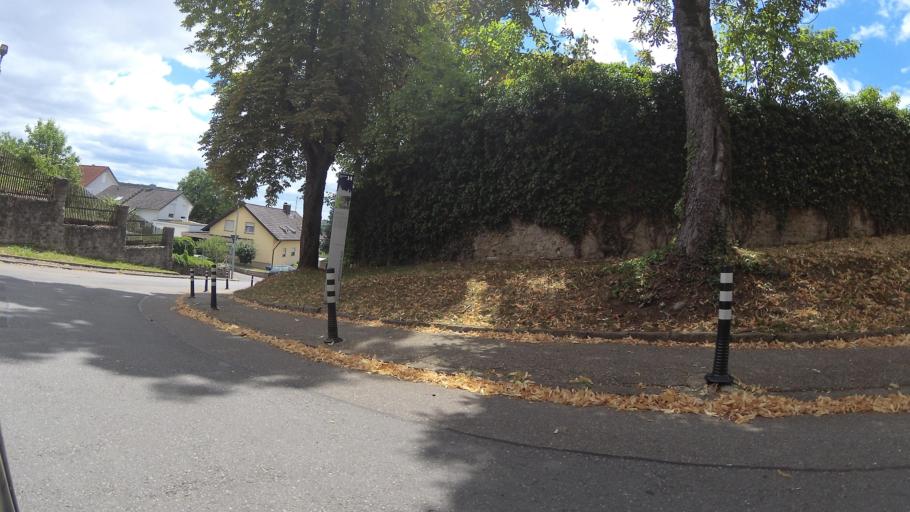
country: DE
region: Baden-Wuerttemberg
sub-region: Regierungsbezirk Stuttgart
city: Gundelsheim
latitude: 49.2882
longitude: 9.1604
